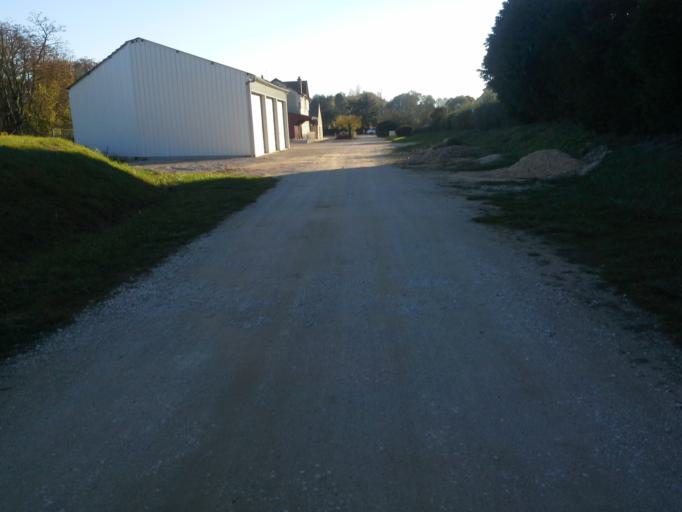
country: FR
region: Centre
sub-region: Departement du Loir-et-Cher
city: Saint-Romain-sur-Cher
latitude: 47.3650
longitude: 1.4010
